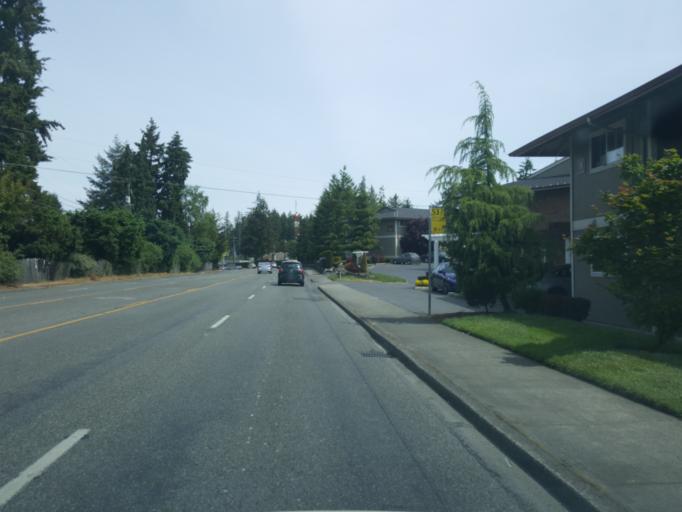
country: US
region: Washington
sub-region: Pierce County
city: Lakewood
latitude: 47.2039
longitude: -122.5072
